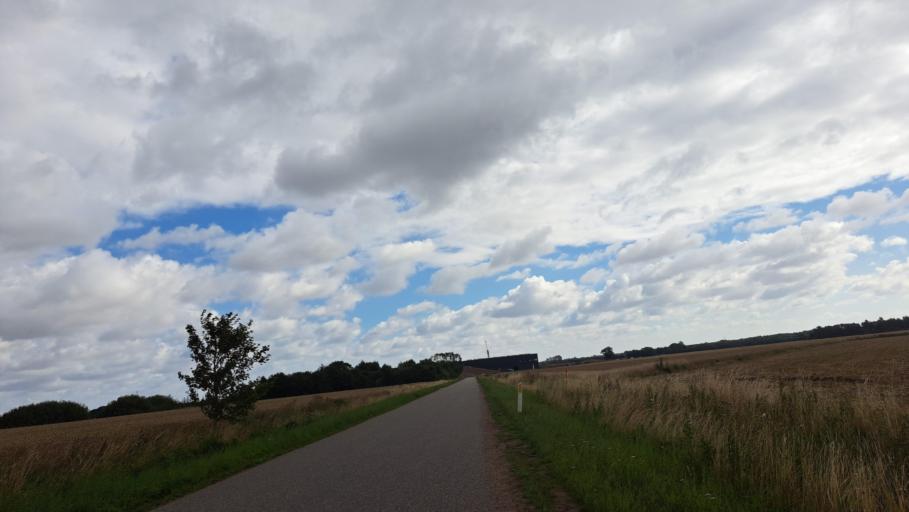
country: DK
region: Central Jutland
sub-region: Hedensted Kommune
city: Hedensted
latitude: 55.7725
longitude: 9.6502
